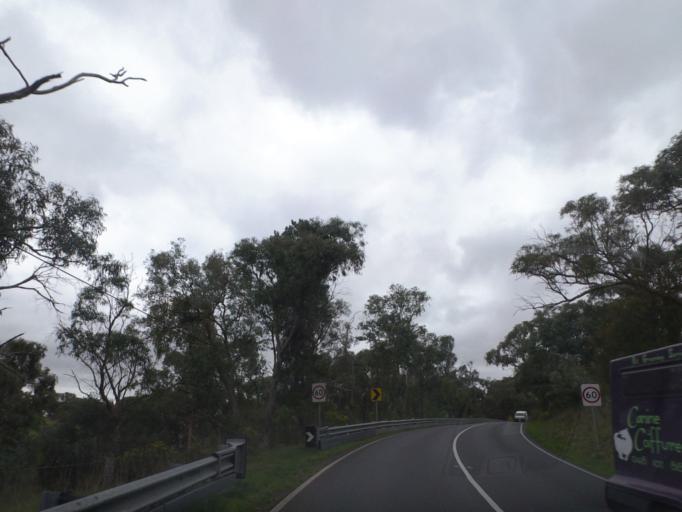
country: AU
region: Victoria
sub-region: Nillumbik
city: Diamond Creek
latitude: -37.6679
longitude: 145.1481
